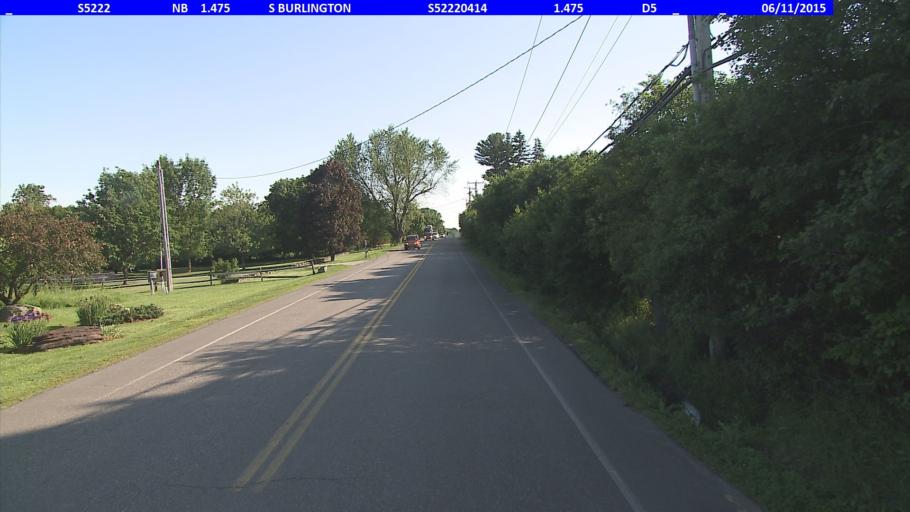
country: US
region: Vermont
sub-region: Chittenden County
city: South Burlington
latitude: 44.4379
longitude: -73.1908
